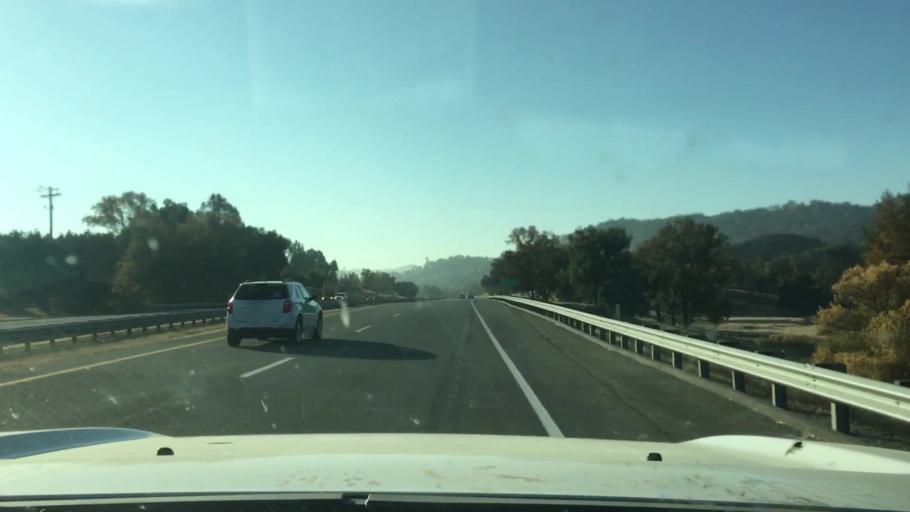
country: US
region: California
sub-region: San Luis Obispo County
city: Santa Margarita
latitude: 35.4393
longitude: -120.6378
